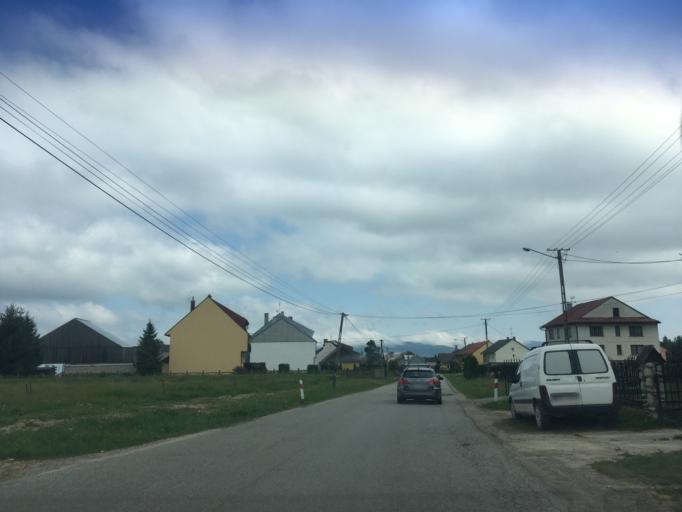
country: PL
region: Lesser Poland Voivodeship
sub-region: Powiat nowotarski
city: Lopuszna
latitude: 49.4348
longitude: 20.1342
